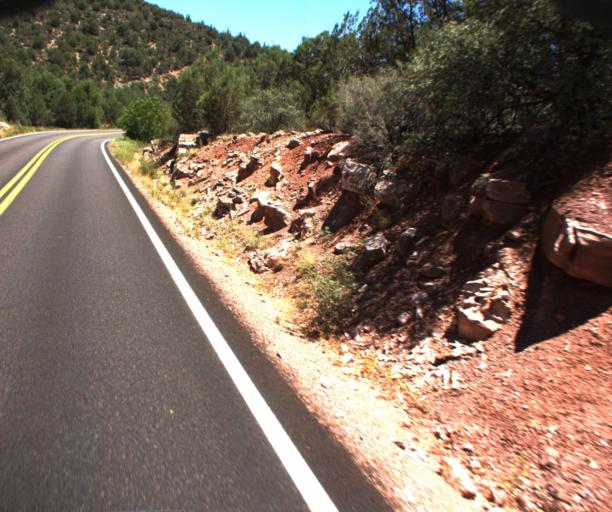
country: US
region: Arizona
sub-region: Gila County
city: Payson
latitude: 34.3098
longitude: -111.3638
